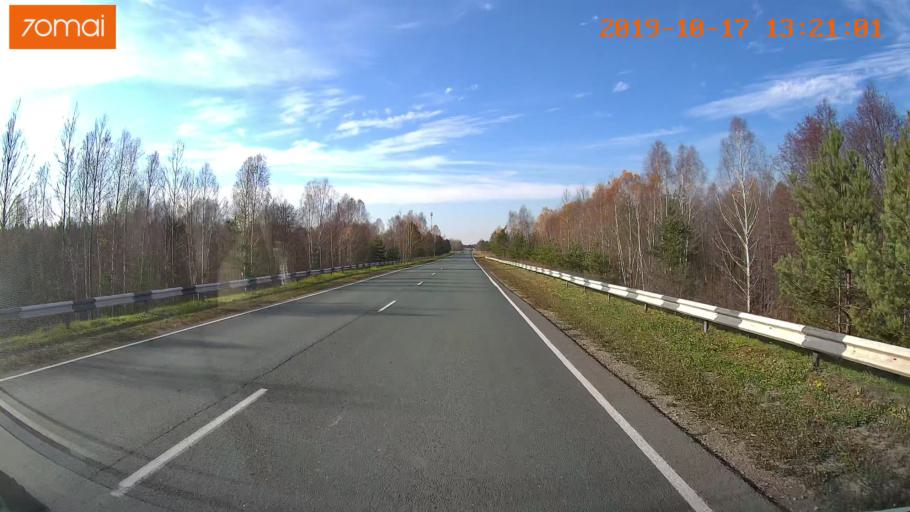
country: RU
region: Rjazan
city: Gus'-Zheleznyy
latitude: 55.0793
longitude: 41.0372
